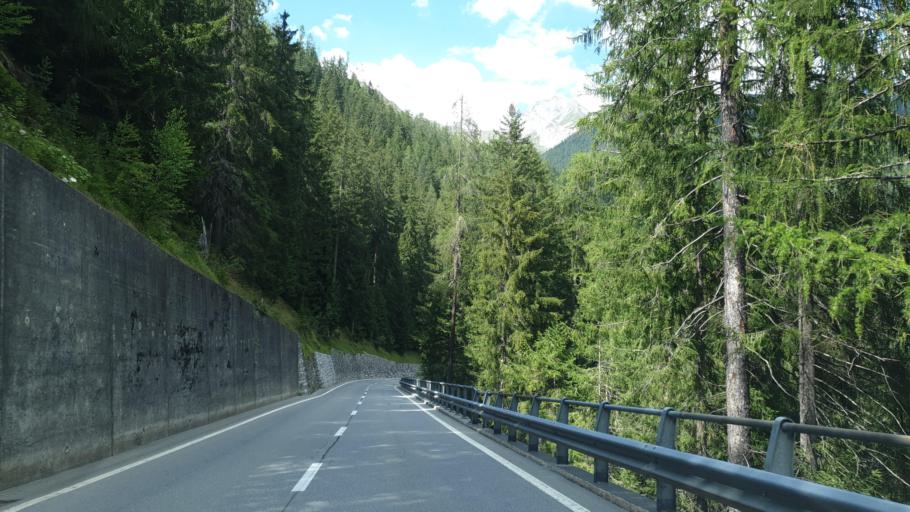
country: CH
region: Grisons
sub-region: Plessur District
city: Arosa
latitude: 46.7016
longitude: 9.7231
